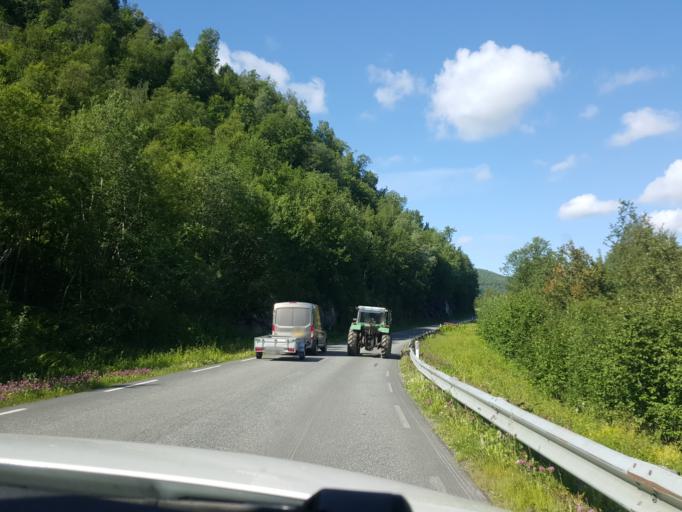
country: NO
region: Nordland
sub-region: Bodo
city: Loding
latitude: 67.1104
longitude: 15.0132
